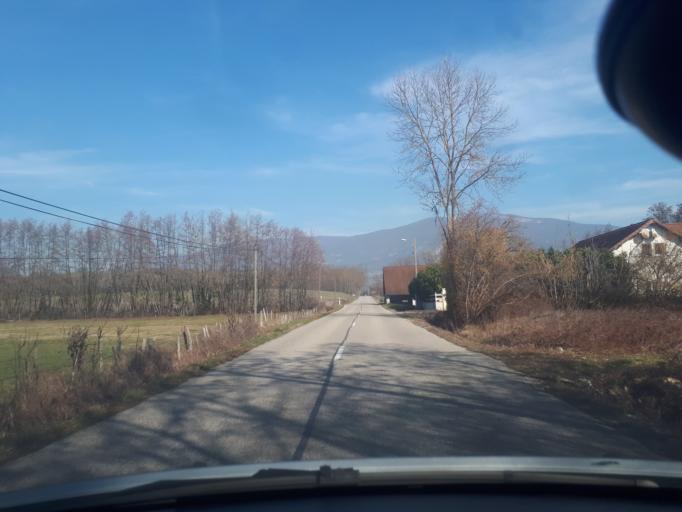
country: FR
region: Rhone-Alpes
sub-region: Departement de l'Isere
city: Creys-Mepieu
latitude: 45.6989
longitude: 5.5308
